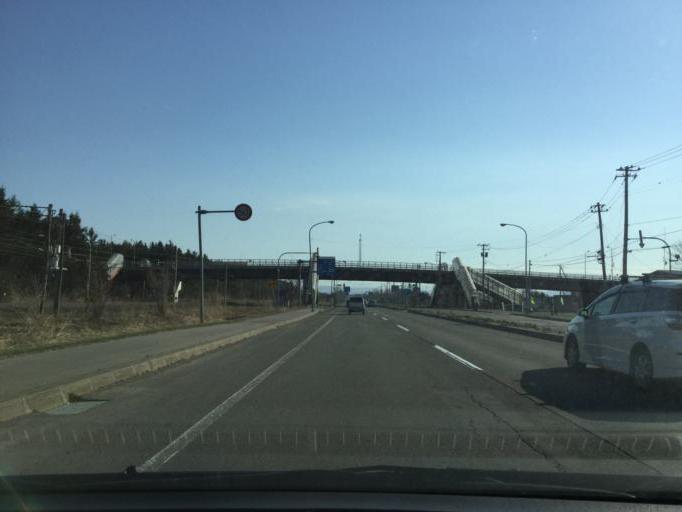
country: JP
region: Hokkaido
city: Iwamizawa
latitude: 43.1766
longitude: 141.7056
